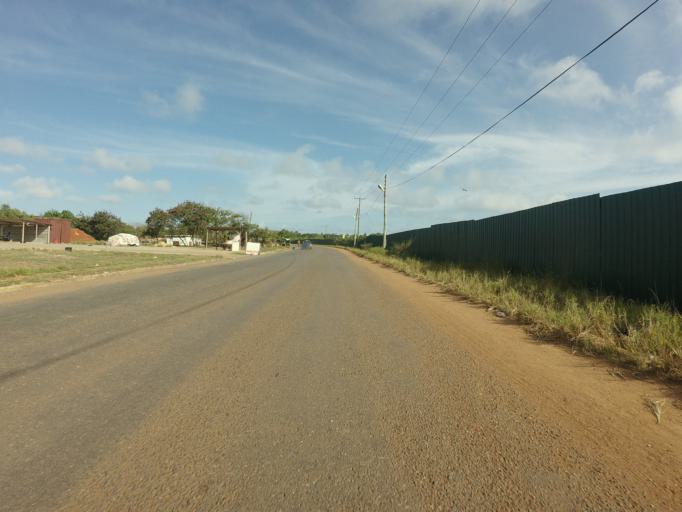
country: GH
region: Greater Accra
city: Teshi Old Town
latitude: 5.5685
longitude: -0.1414
